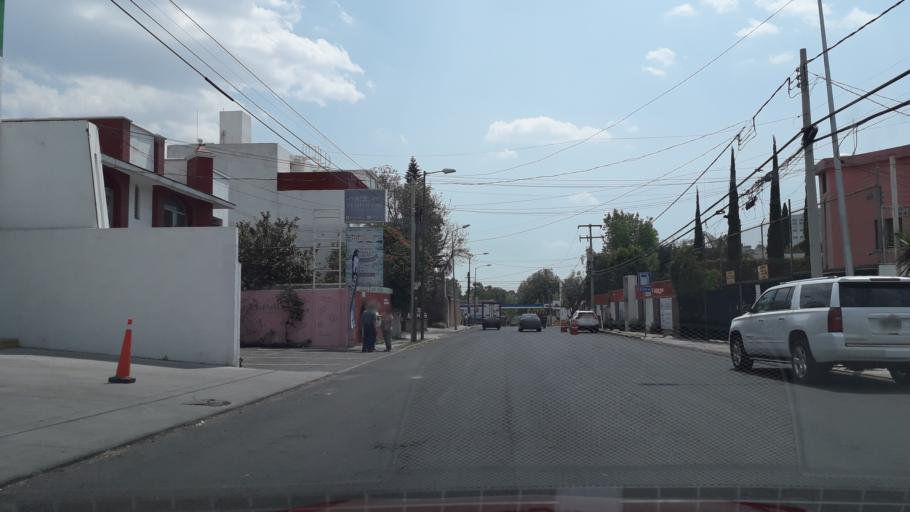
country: MX
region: Puebla
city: Puebla
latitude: 19.0327
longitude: -98.2227
